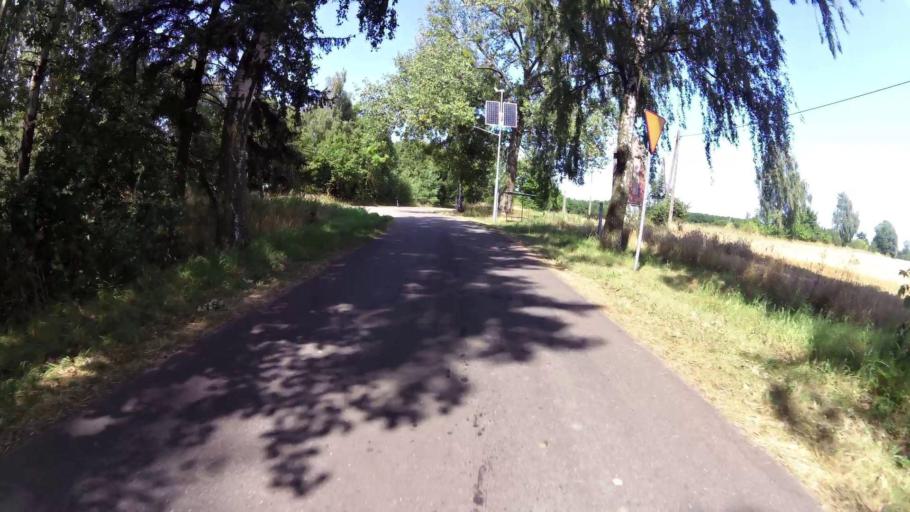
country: PL
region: West Pomeranian Voivodeship
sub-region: Powiat stargardzki
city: Suchan
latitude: 53.2958
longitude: 15.3652
